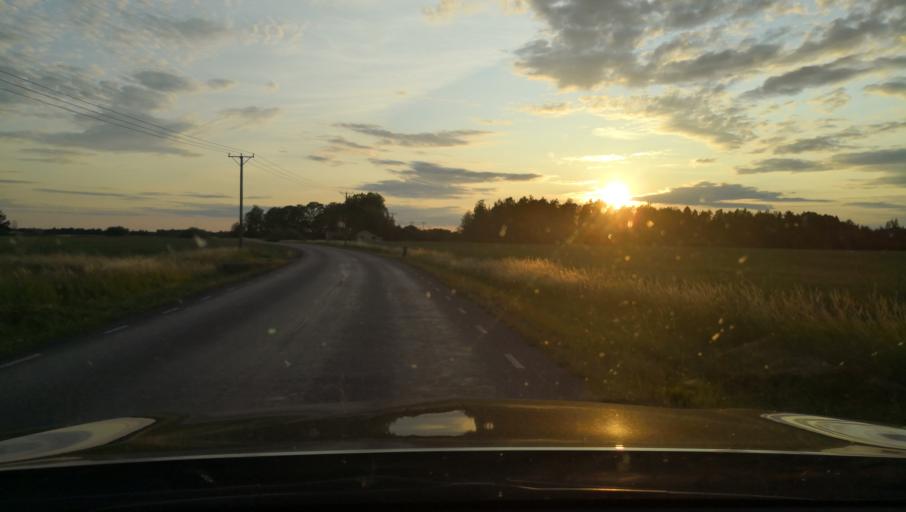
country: SE
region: Uppsala
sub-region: Uppsala Kommun
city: Vattholma
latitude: 60.0220
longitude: 17.6949
